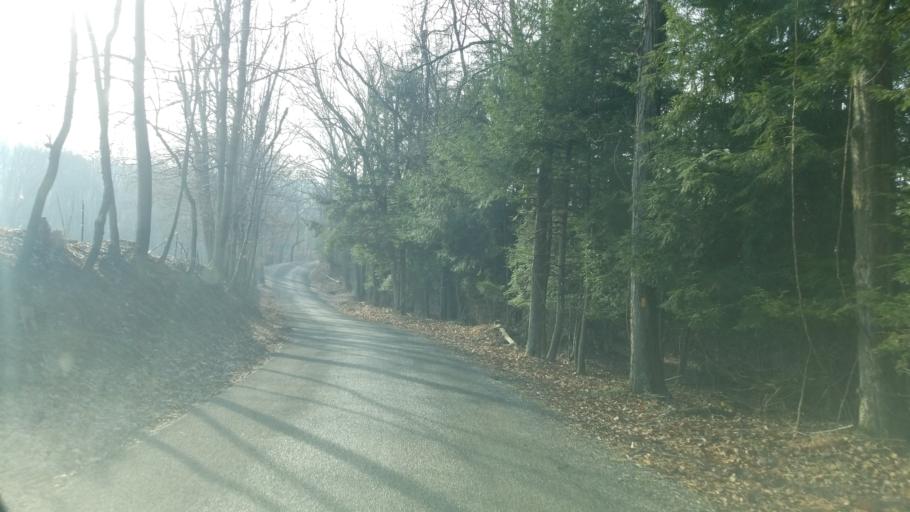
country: US
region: Pennsylvania
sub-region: Jefferson County
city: Brookville
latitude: 40.9574
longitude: -79.2642
